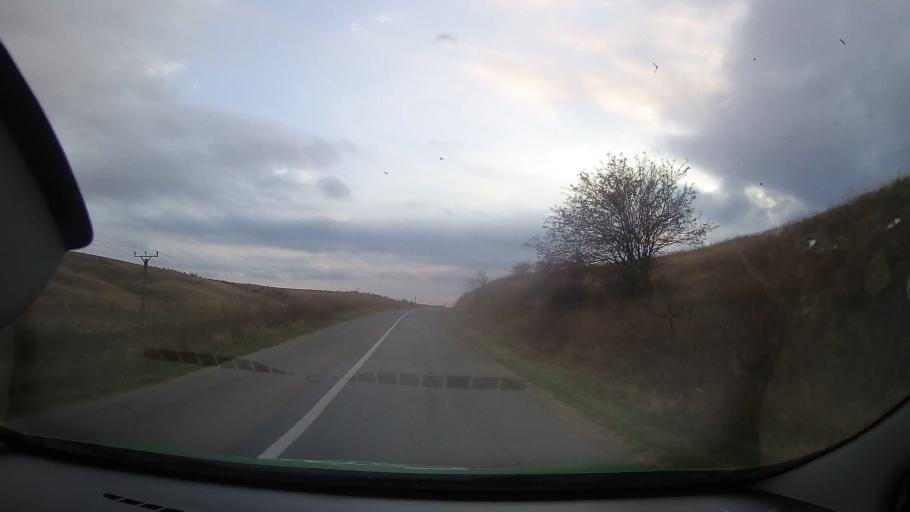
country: RO
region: Constanta
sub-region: Comuna Dobromir
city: Dobromir
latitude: 44.0326
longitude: 27.8012
